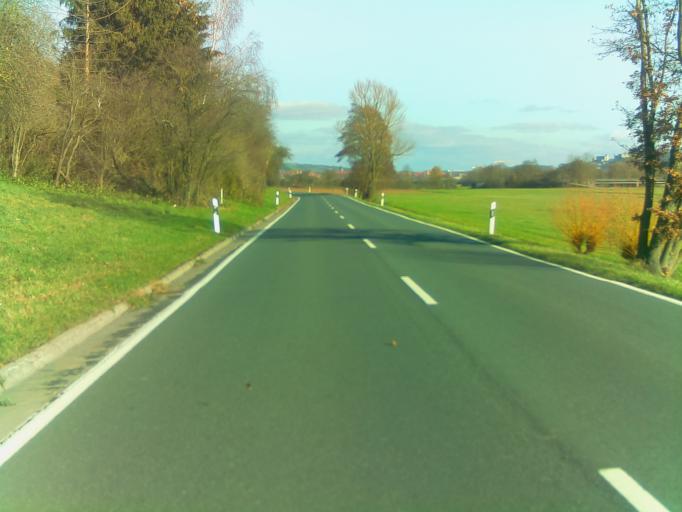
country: DE
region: Bavaria
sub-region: Regierungsbezirk Unterfranken
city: Hohenroth
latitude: 50.3080
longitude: 10.1853
